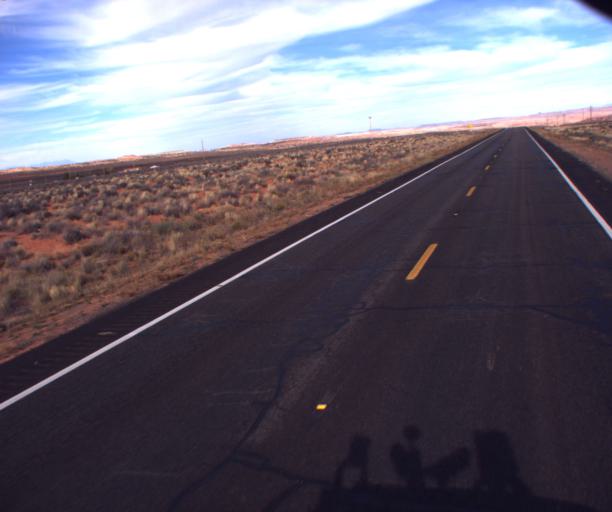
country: US
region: Arizona
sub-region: Navajo County
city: Kayenta
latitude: 36.9171
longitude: -109.7703
